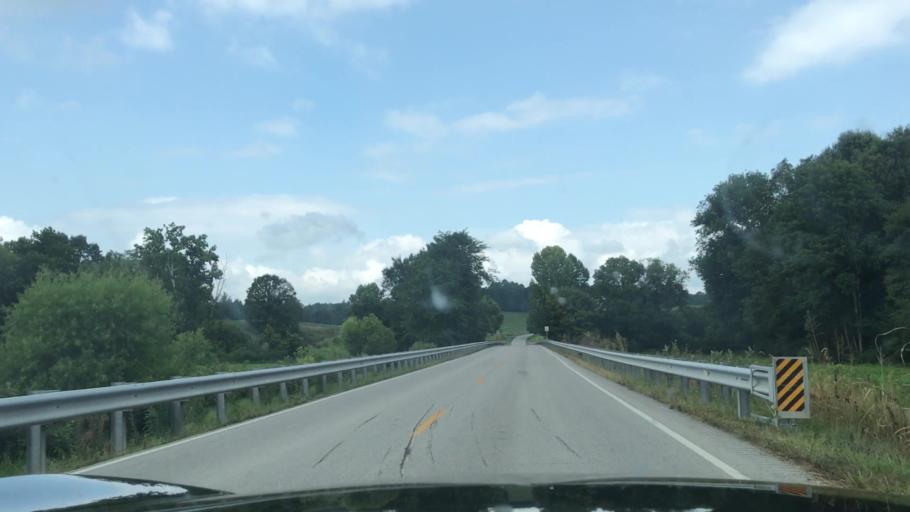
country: US
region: Kentucky
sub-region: Butler County
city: Morgantown
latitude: 37.1760
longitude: -86.8458
